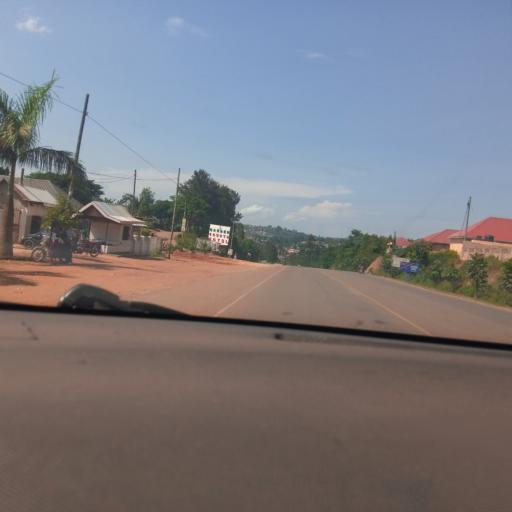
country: UG
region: Central Region
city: Masaka
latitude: -0.3133
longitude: 31.7463
